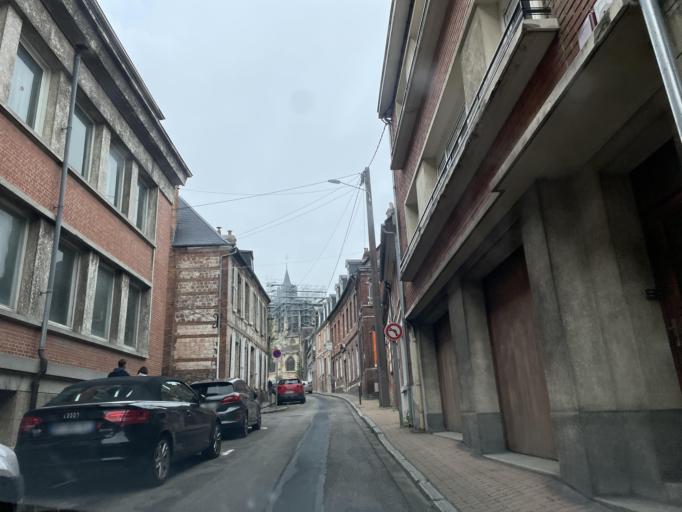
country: FR
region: Haute-Normandie
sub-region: Departement de la Seine-Maritime
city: Eu
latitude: 50.0477
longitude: 1.4216
